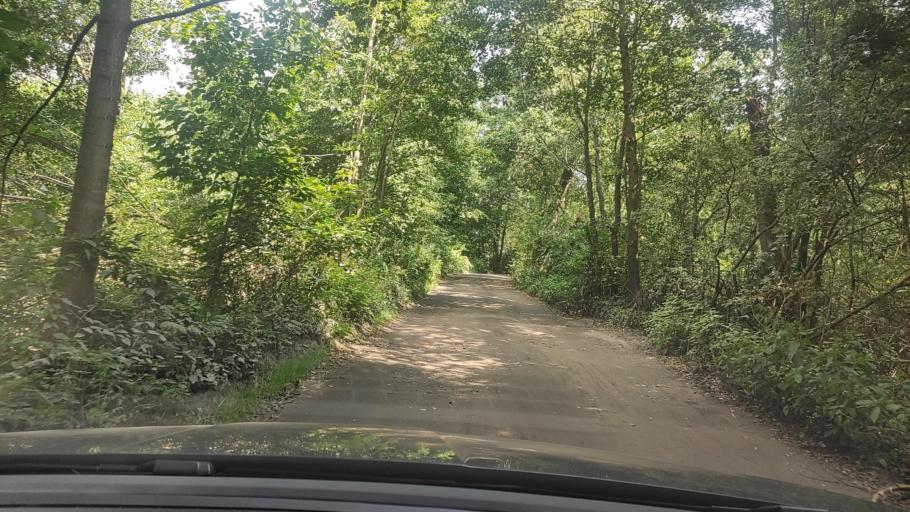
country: PL
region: Greater Poland Voivodeship
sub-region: Powiat poznanski
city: Pobiedziska
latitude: 52.5039
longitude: 17.2040
